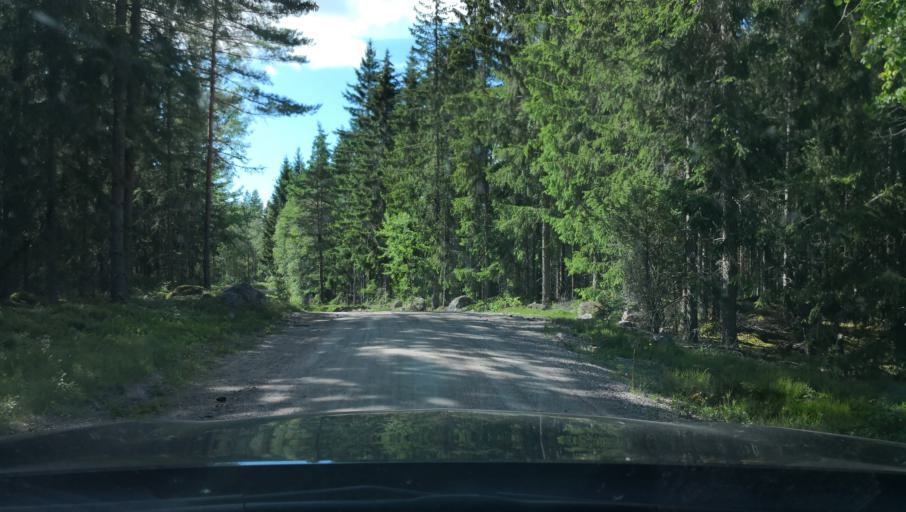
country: SE
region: Vaestmanland
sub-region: Kungsors Kommun
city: Kungsoer
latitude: 59.3275
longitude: 16.0333
